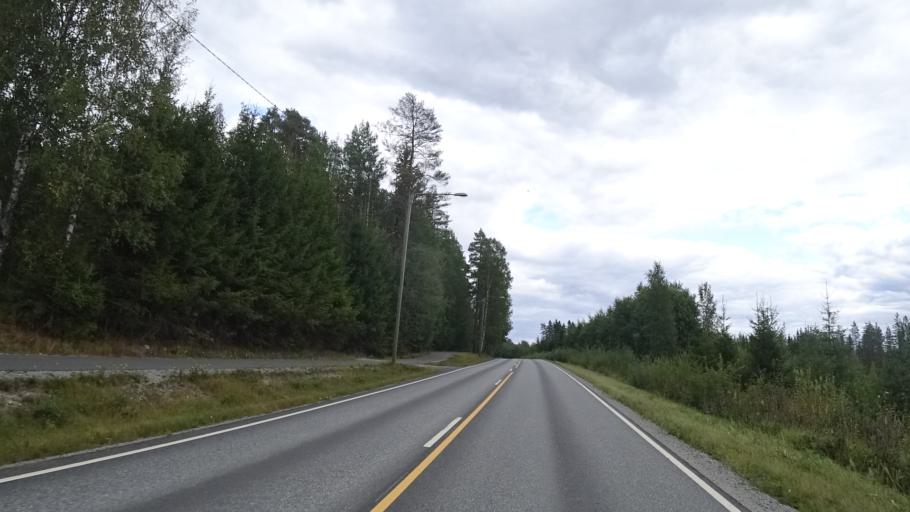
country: FI
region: North Karelia
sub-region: Joensuu
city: Ilomantsi
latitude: 62.6538
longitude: 30.9546
